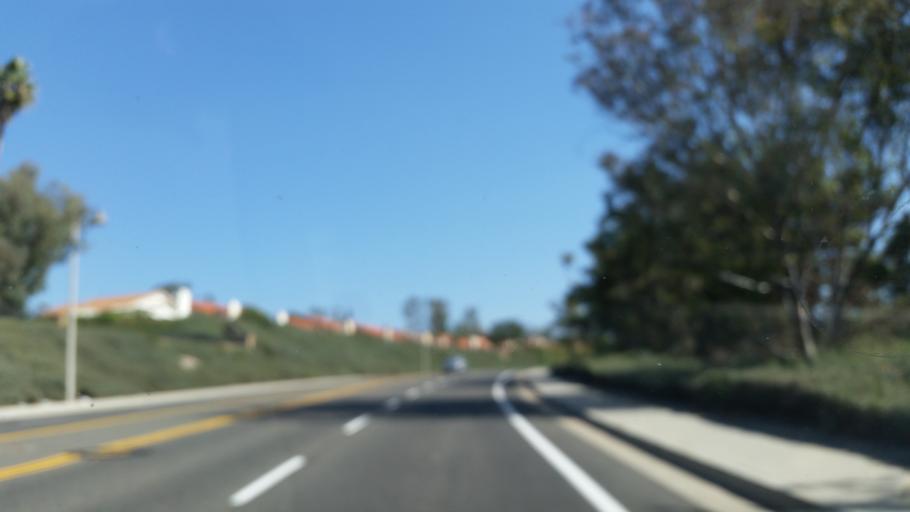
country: US
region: California
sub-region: Orange County
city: Las Flores
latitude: 33.6149
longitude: -117.6382
